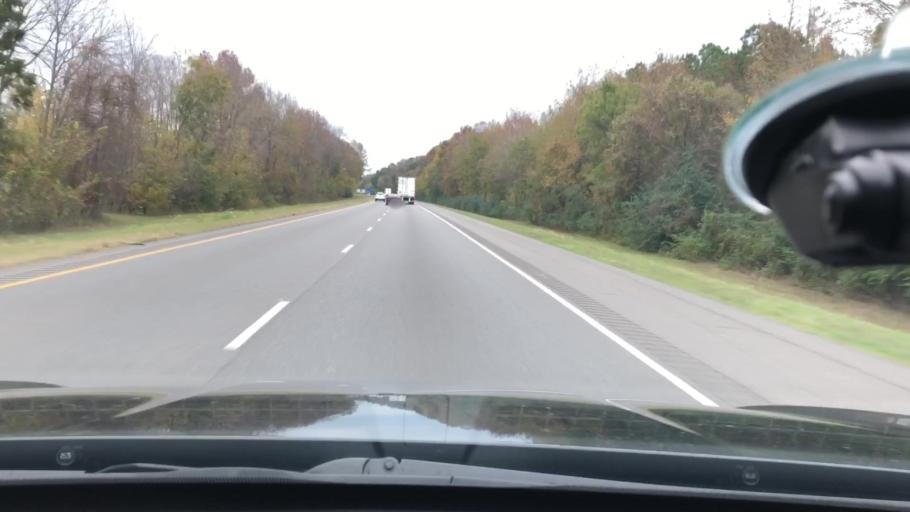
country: US
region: Arkansas
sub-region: Hempstead County
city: Hope
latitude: 33.6597
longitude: -93.6453
